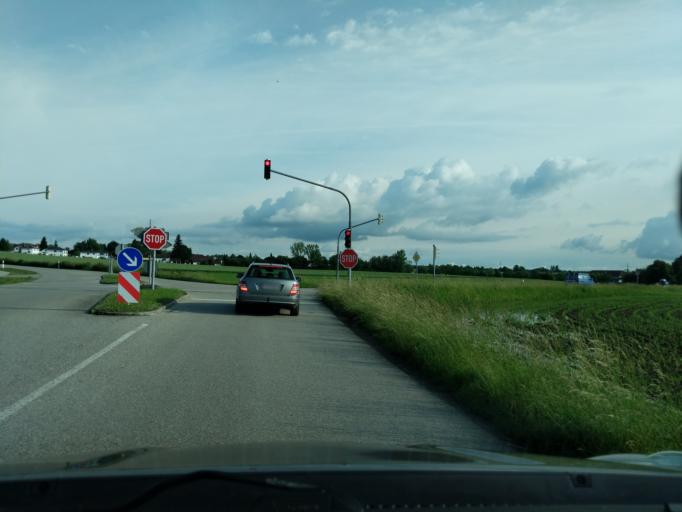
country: DE
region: Bavaria
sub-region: Upper Bavaria
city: Zorneding
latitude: 48.0985
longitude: 11.8257
